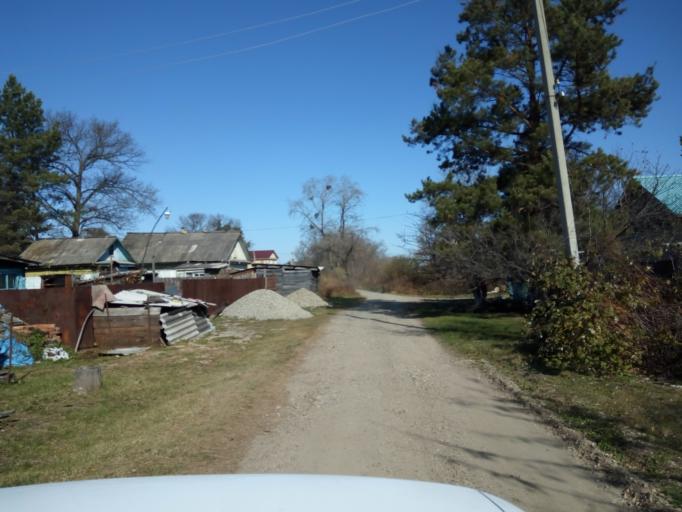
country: RU
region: Primorskiy
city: Dal'nerechensk
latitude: 45.9089
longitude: 133.7954
